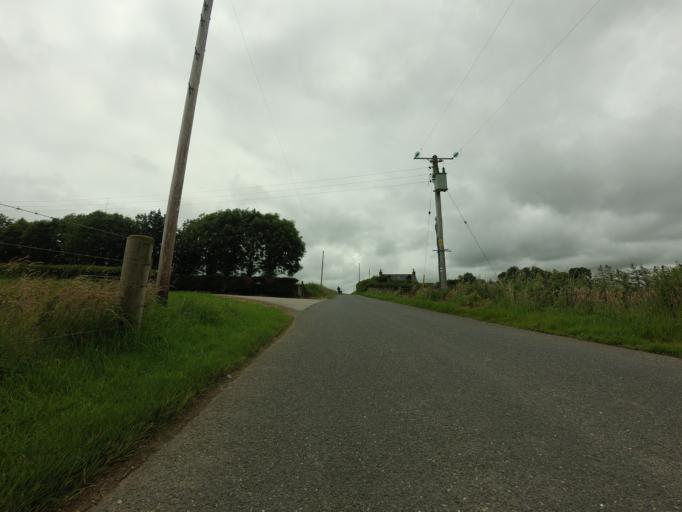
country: GB
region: Scotland
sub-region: Aberdeenshire
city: Turriff
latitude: 57.5352
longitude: -2.4313
